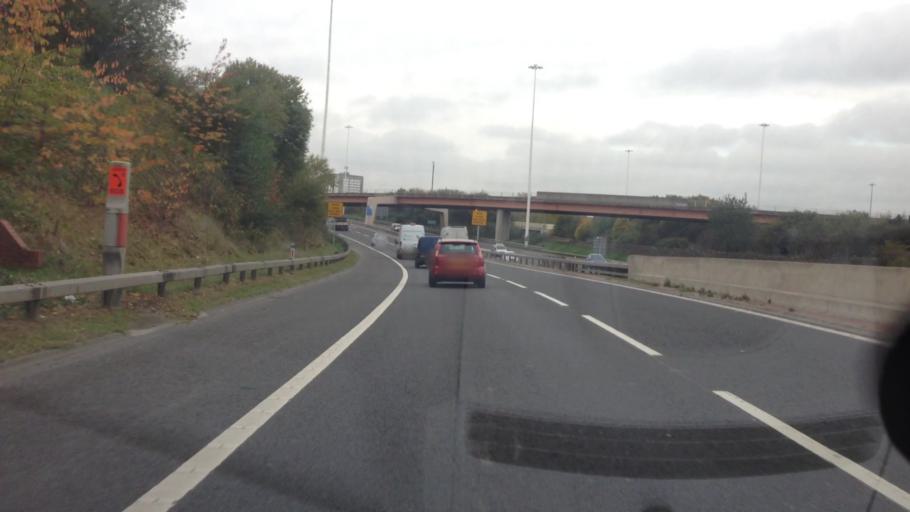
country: GB
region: England
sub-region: City and Borough of Leeds
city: Leeds
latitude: 53.7840
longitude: -1.5448
